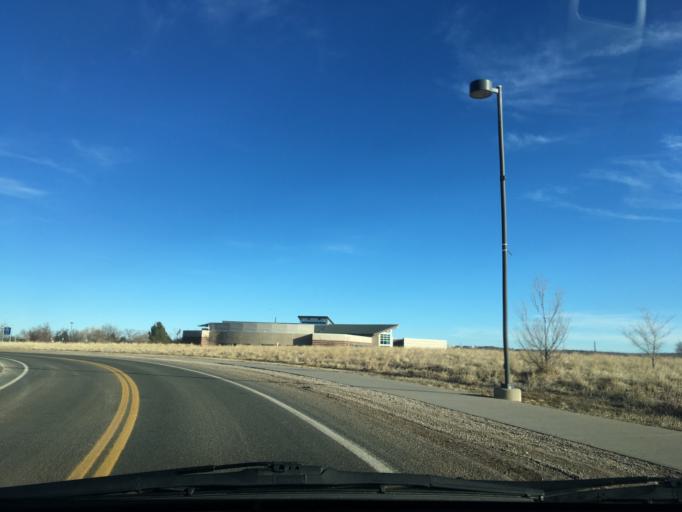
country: US
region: Colorado
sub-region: Broomfield County
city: Broomfield
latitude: 39.9354
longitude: -105.0384
